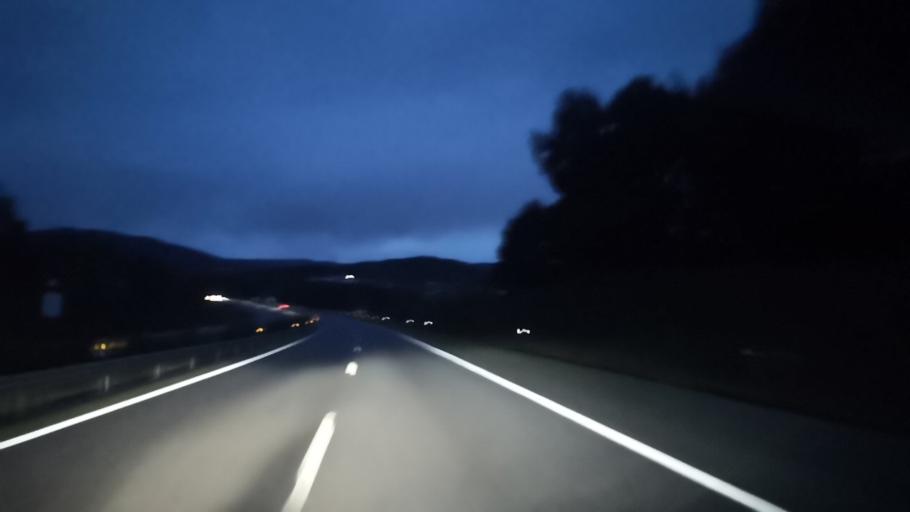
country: PT
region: Braga
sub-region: Guimaraes
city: Ponte
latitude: 41.4539
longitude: -8.3400
